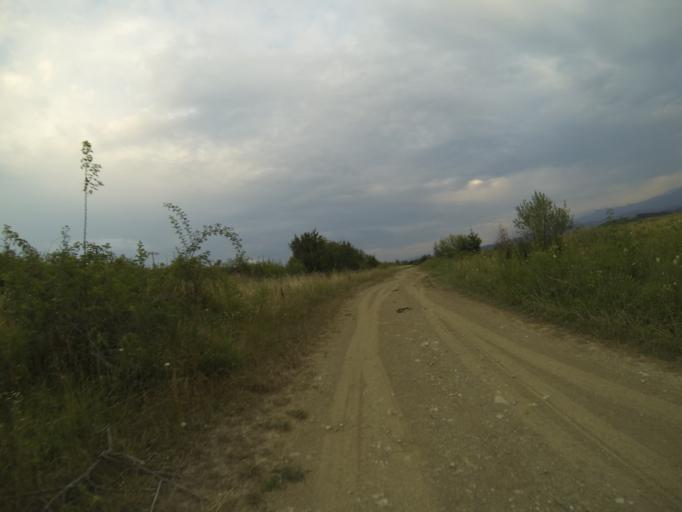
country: RO
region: Brasov
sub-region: Comuna Sinca Veche
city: Sinca Veche
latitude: 45.7752
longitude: 25.1664
